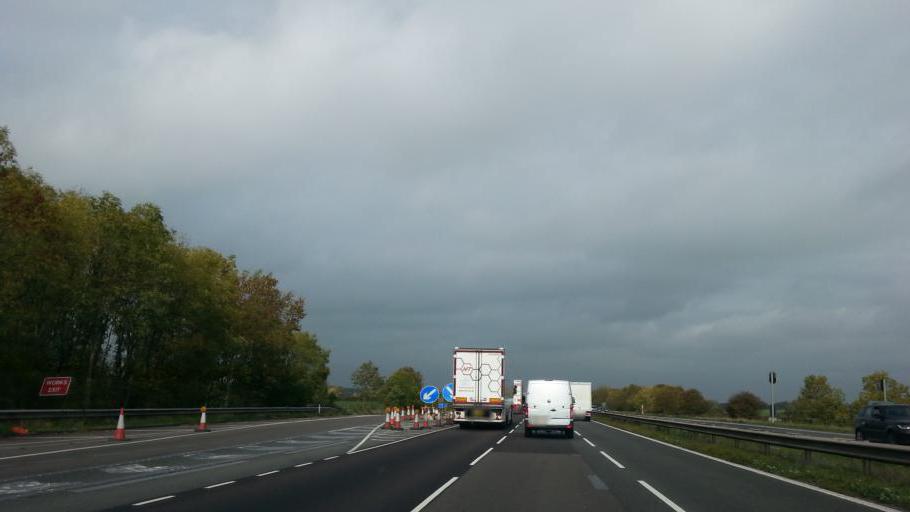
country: GB
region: England
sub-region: Staffordshire
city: Audley
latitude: 53.0634
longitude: -2.3322
